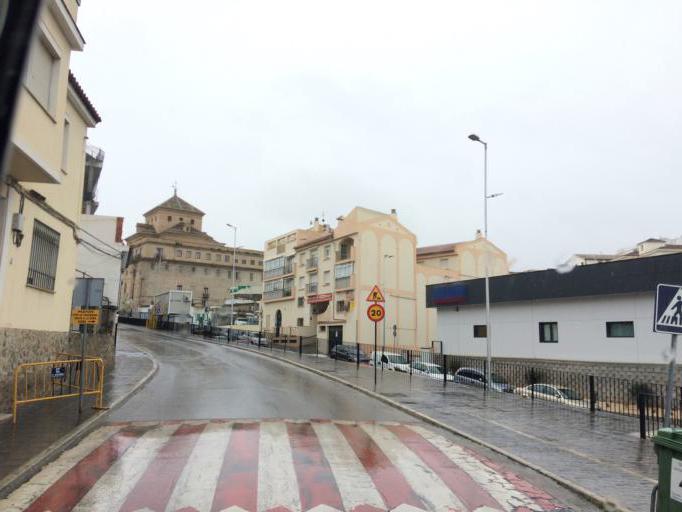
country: ES
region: Andalusia
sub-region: Provincia de Malaga
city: Antequera
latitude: 37.0243
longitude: -4.5598
